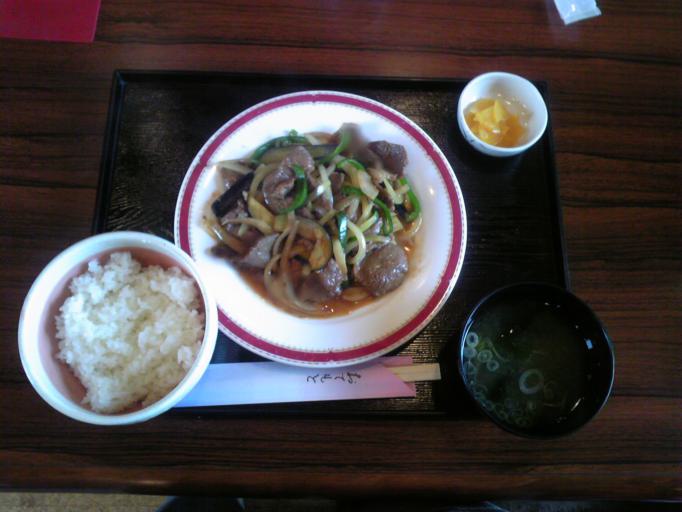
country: JP
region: Hokkaido
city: Kushiro
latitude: 43.0740
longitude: 144.3200
